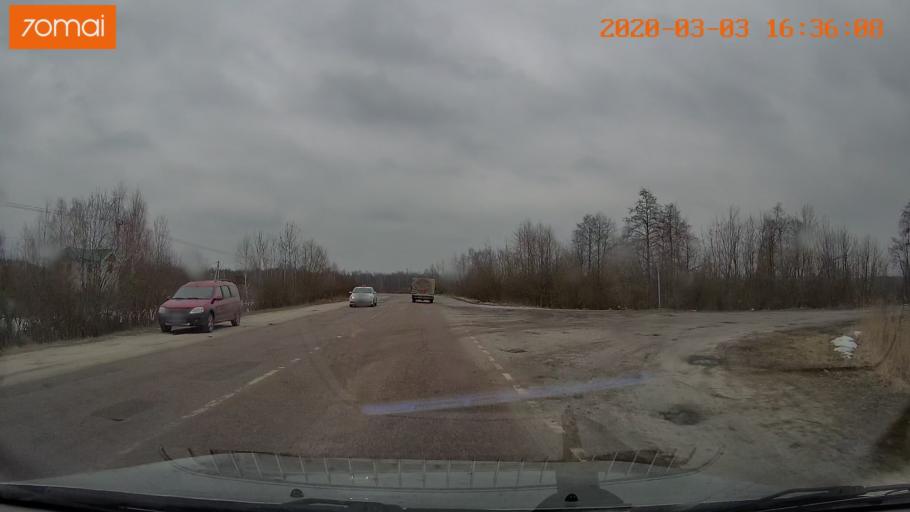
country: RU
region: Moskovskaya
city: Lopatinskiy
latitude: 55.4003
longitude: 38.7693
